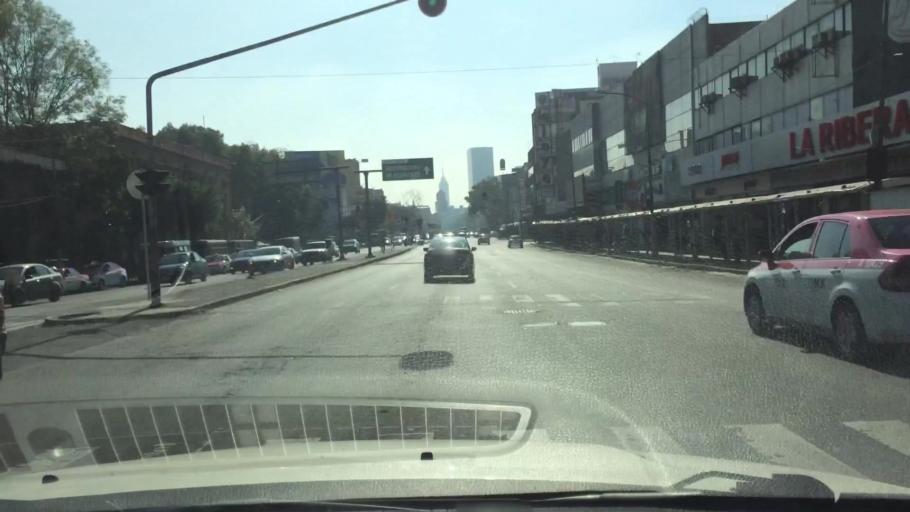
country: MX
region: Mexico City
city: Cuauhtemoc
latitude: 19.4418
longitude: -99.1606
